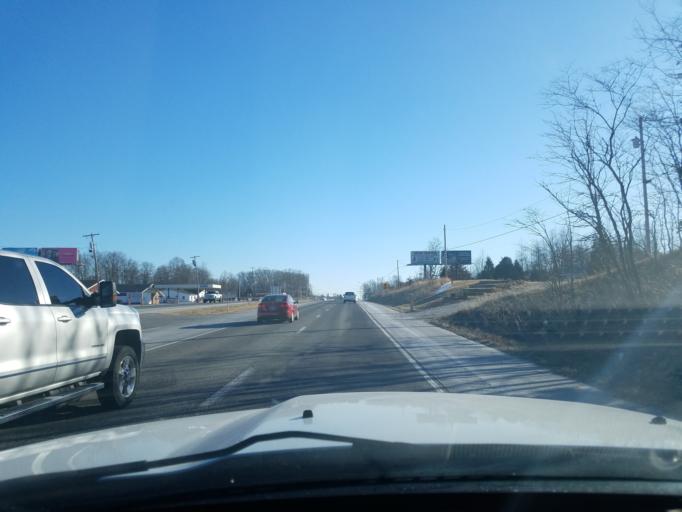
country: US
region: Indiana
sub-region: Lawrence County
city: Bedford
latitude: 38.8164
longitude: -86.5183
